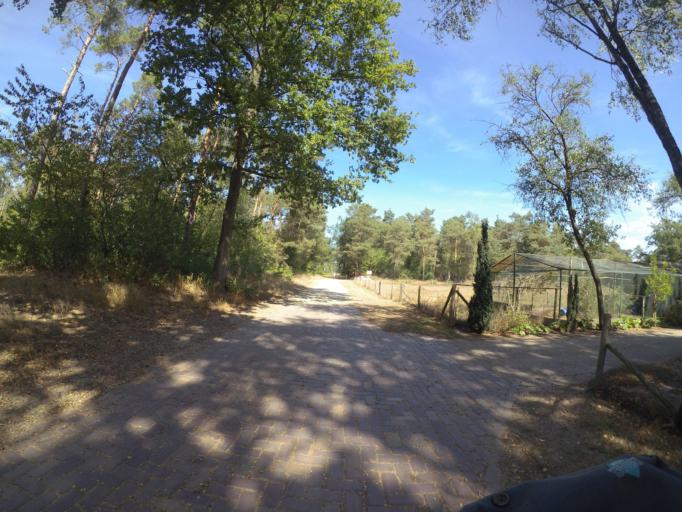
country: NL
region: Overijssel
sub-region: Gemeente Twenterand
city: Den Ham
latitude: 52.3742
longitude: 6.4117
